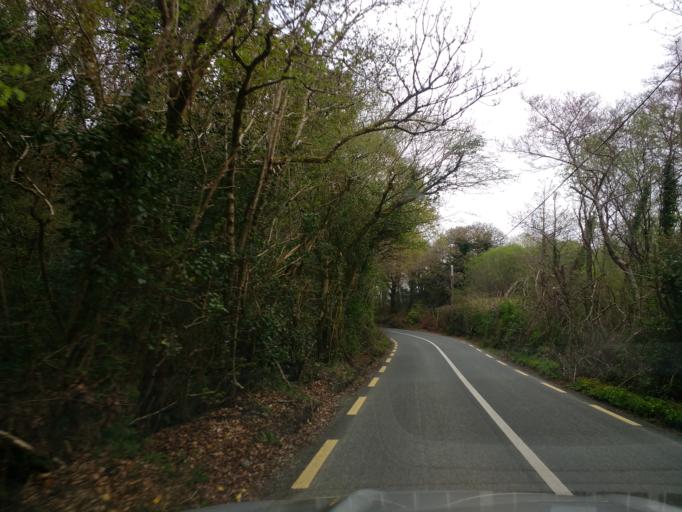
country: IE
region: Ulster
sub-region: County Donegal
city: Buncrana
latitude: 55.1286
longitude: -7.5289
